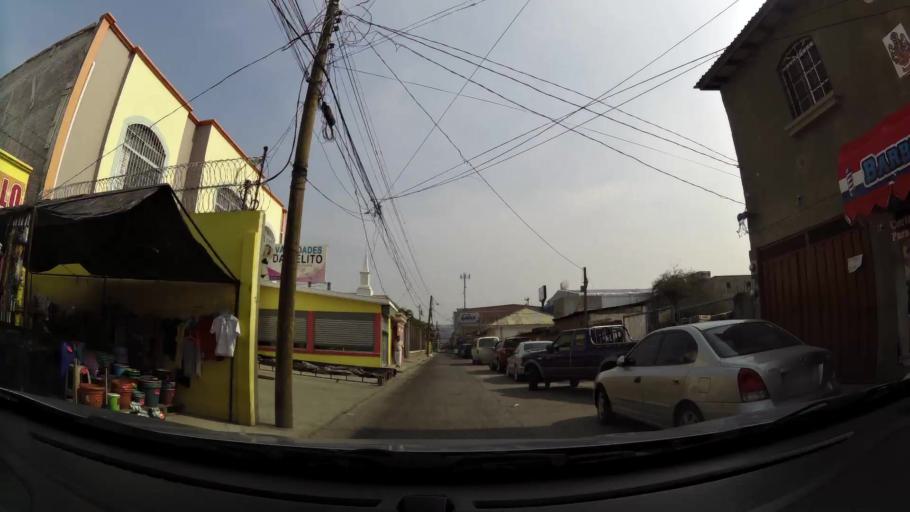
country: HN
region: Comayagua
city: Comayagua
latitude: 14.4543
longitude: -87.6421
